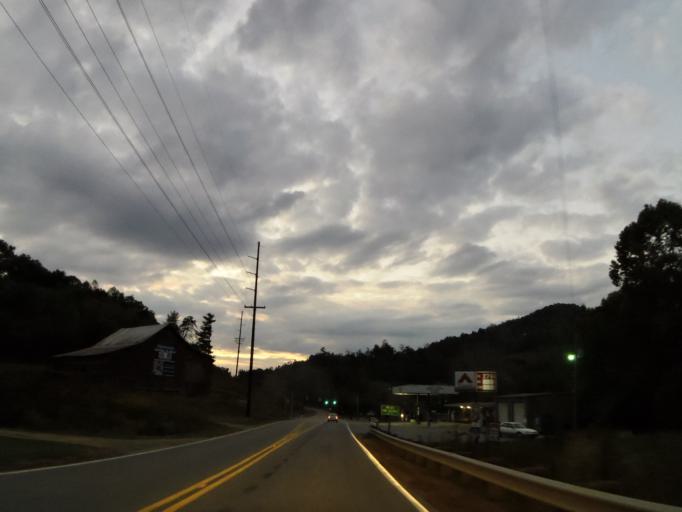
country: US
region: North Carolina
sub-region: Madison County
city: Marshall
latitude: 35.8378
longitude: -82.7154
